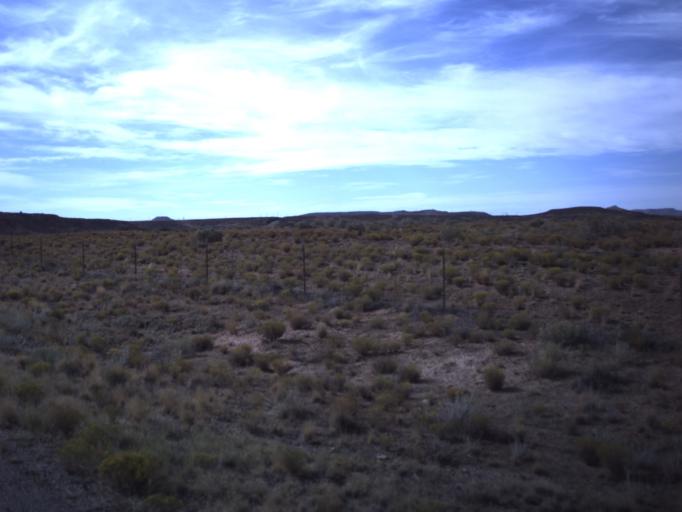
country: US
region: Utah
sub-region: San Juan County
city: Blanding
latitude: 37.3033
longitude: -109.2842
